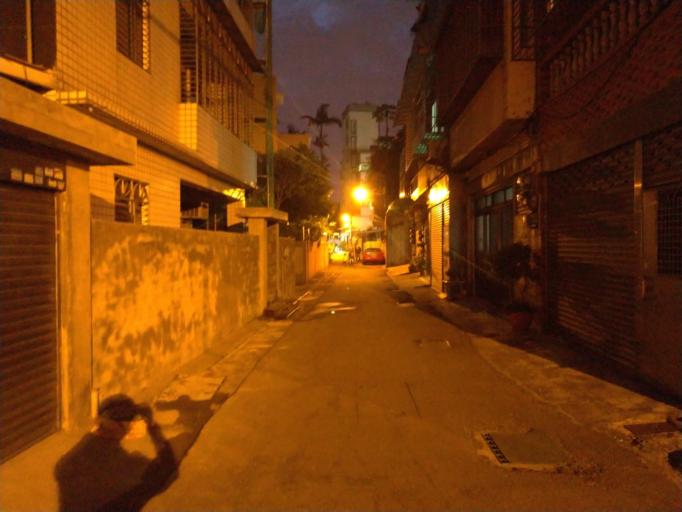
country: TW
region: Taiwan
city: Taoyuan City
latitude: 24.9751
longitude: 121.2544
